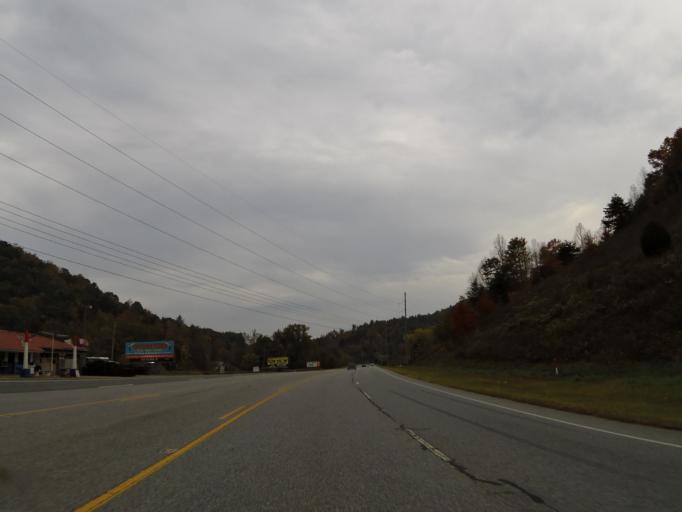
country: US
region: North Carolina
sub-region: Caldwell County
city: Lenoir
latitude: 36.0149
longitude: -81.5714
